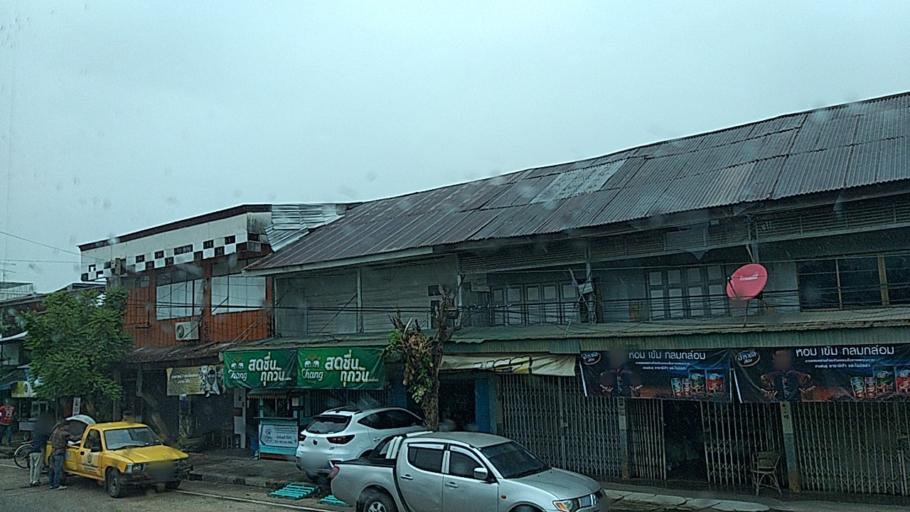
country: TH
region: Maha Sarakham
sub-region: Amphoe Borabue
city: Borabue
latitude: 16.0389
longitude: 103.1211
